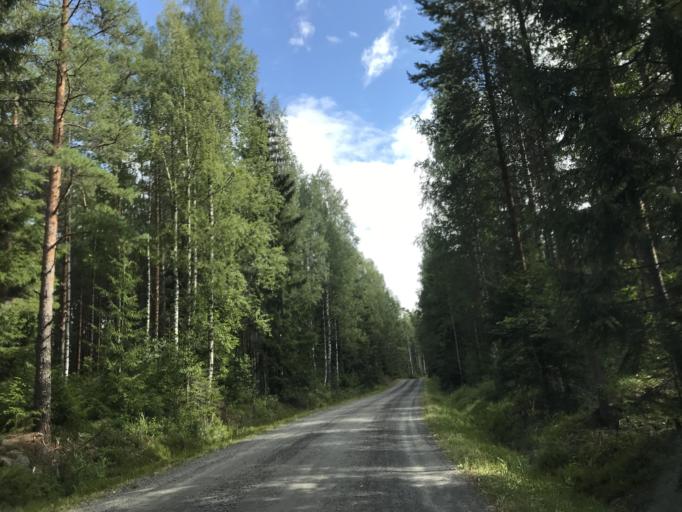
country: FI
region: Uusimaa
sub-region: Helsinki
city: Kaerkoelae
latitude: 60.6355
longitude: 23.8016
